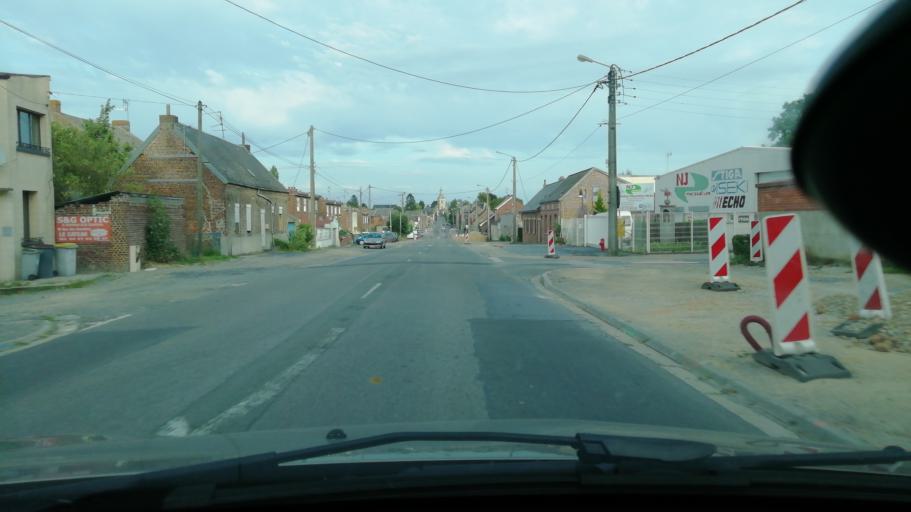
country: FR
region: Nord-Pas-de-Calais
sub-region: Departement du Nord
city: Viesly
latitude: 50.1251
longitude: 3.4507
